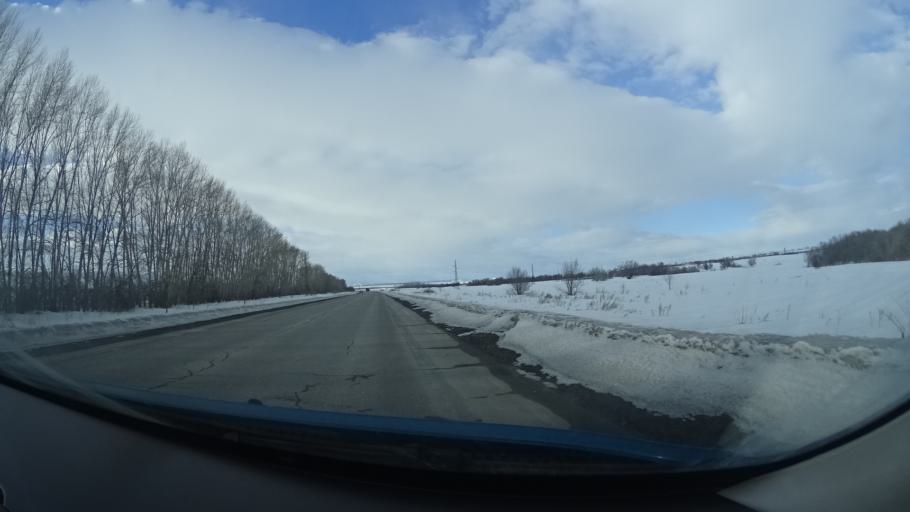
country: RU
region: Chelyabinsk
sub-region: Gorod Magnitogorsk
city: Magnitogorsk
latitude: 53.5725
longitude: 58.8939
